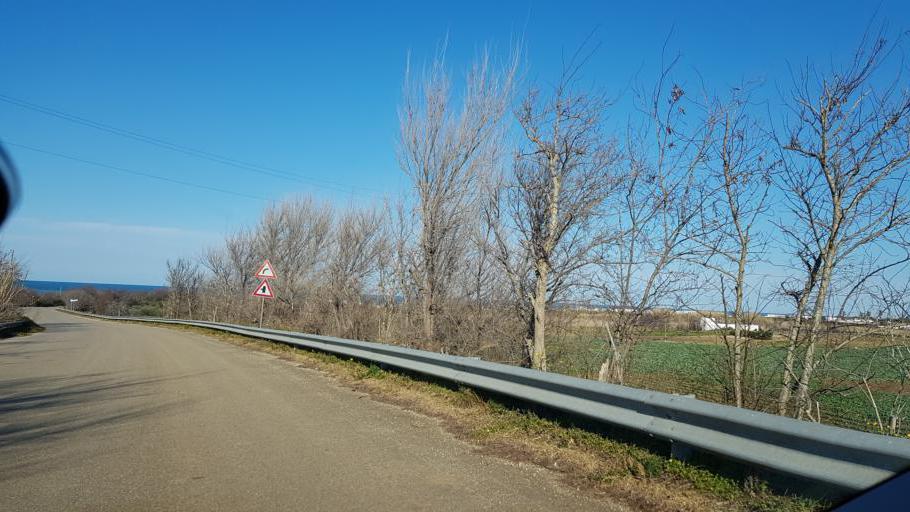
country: IT
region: Apulia
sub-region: Provincia di Brindisi
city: San Vito dei Normanni
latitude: 40.6911
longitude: 17.8261
